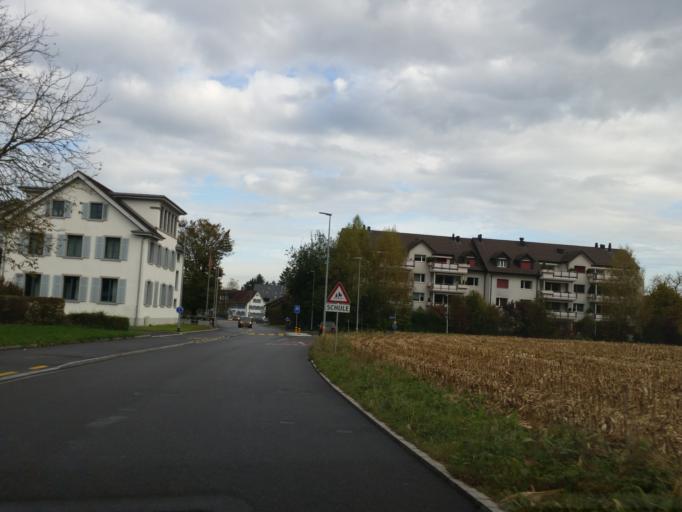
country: CH
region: Zurich
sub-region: Bezirk Uster
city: Duebendorf / Vogelquartier
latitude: 47.3883
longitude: 8.6157
